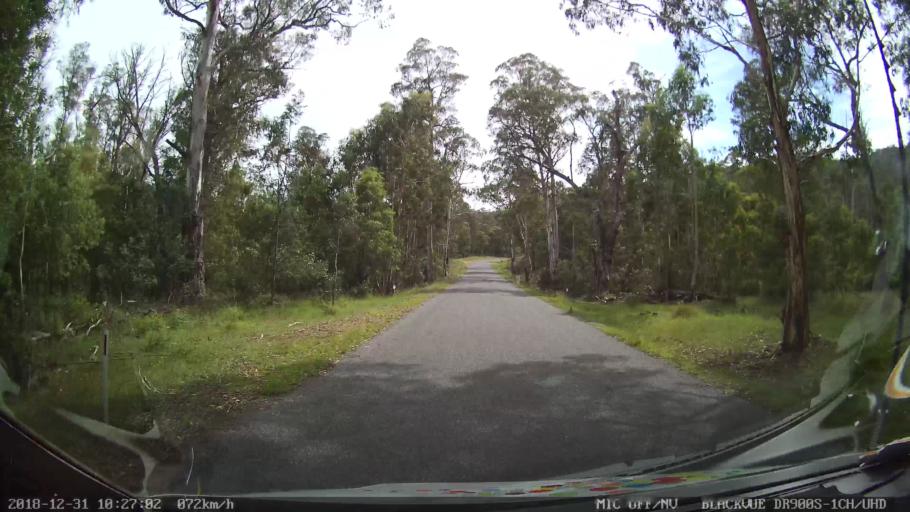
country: AU
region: New South Wales
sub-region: Snowy River
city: Jindabyne
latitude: -36.4894
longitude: 148.1407
